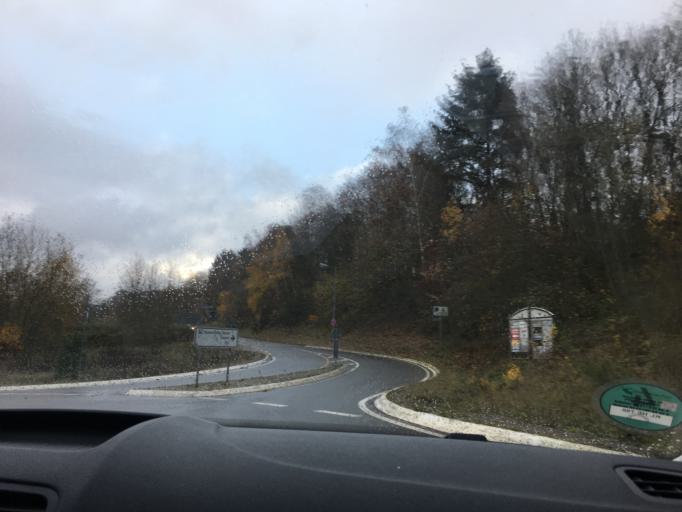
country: DE
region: Rheinland-Pfalz
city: Pirmasens
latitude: 49.2147
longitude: 7.6050
